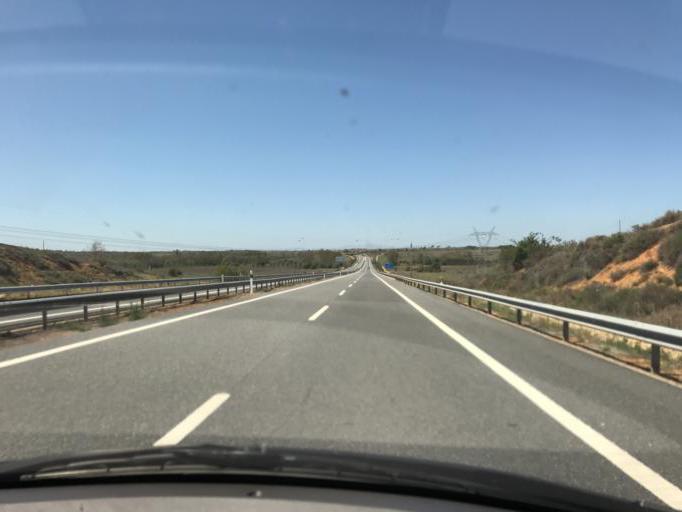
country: ES
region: Castille and Leon
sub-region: Provincia de Leon
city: Valverde de la Virgen
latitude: 42.5637
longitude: -5.6691
